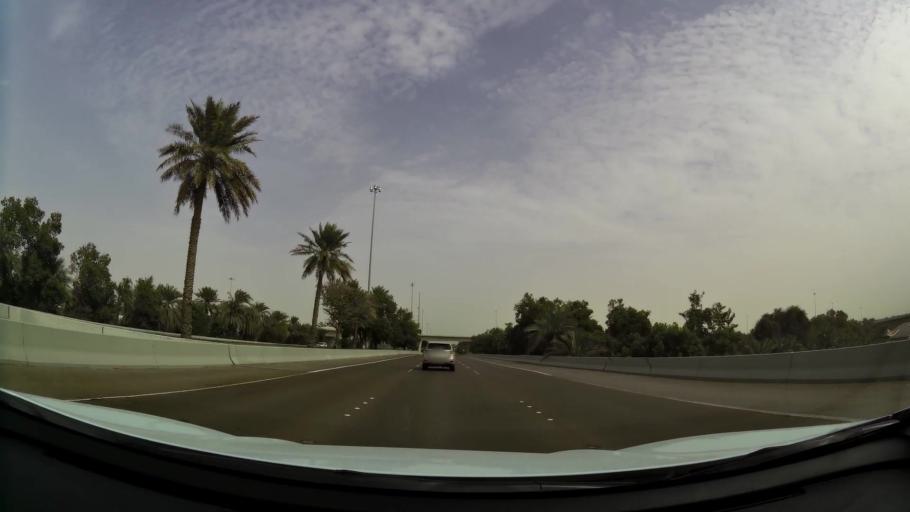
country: AE
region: Abu Dhabi
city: Abu Dhabi
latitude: 24.3905
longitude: 54.5390
